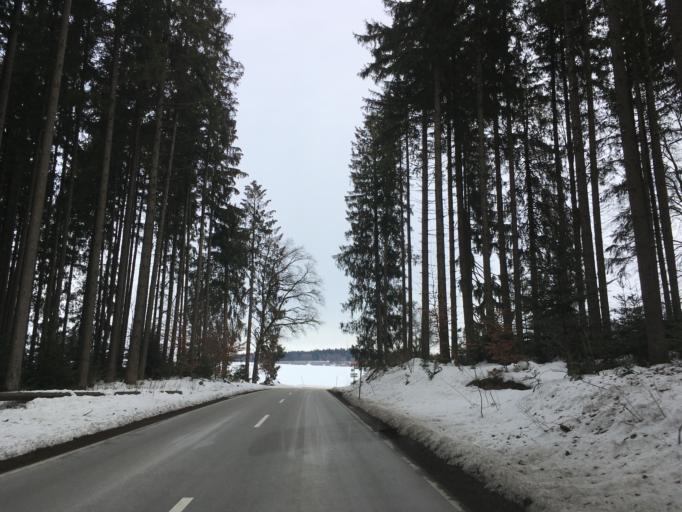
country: DE
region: Bavaria
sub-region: Upper Bavaria
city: Schnaitsee
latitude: 48.0577
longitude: 12.3535
